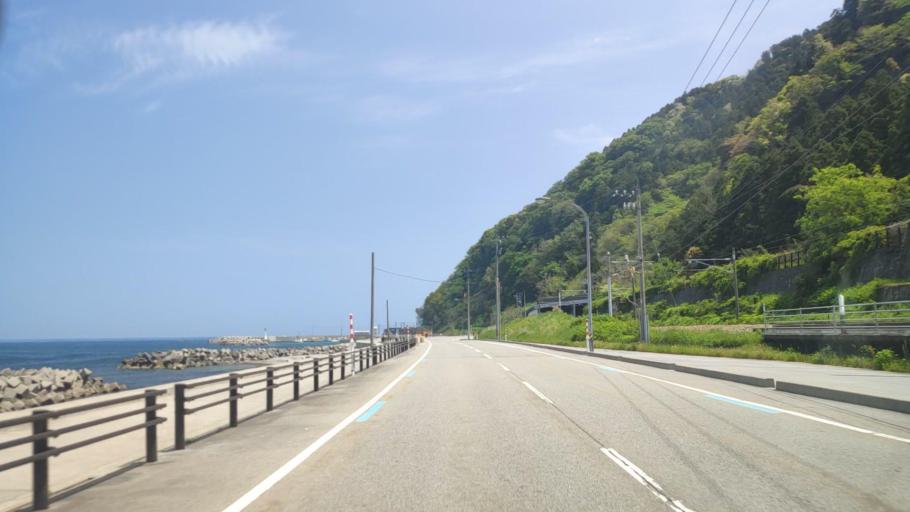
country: JP
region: Toyama
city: Nyuzen
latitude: 36.9688
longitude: 137.5816
